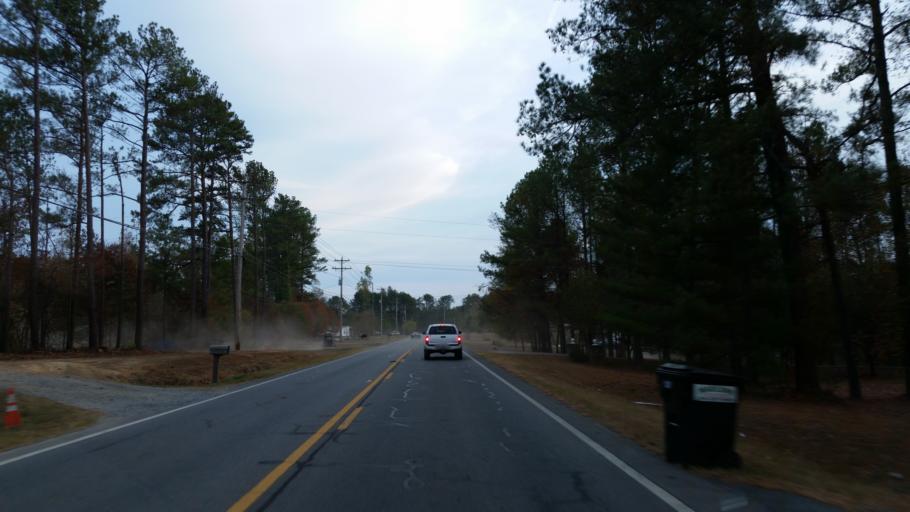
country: US
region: Georgia
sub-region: Gordon County
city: Calhoun
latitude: 34.5985
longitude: -84.9117
